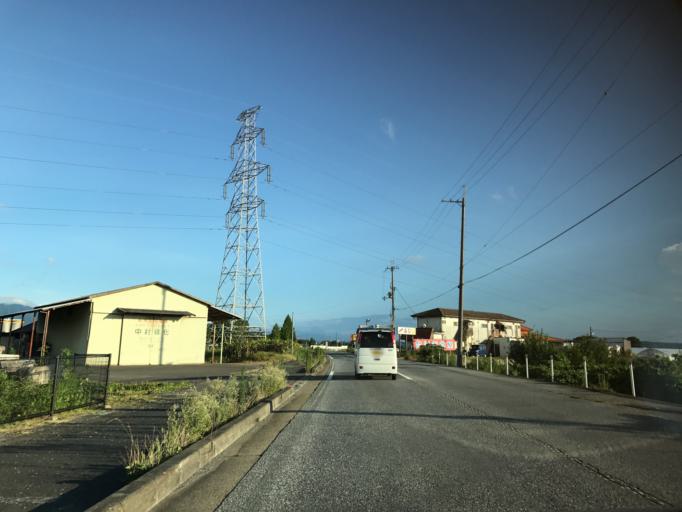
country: JP
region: Shiga Prefecture
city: Youkaichi
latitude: 35.1129
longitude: 136.2571
